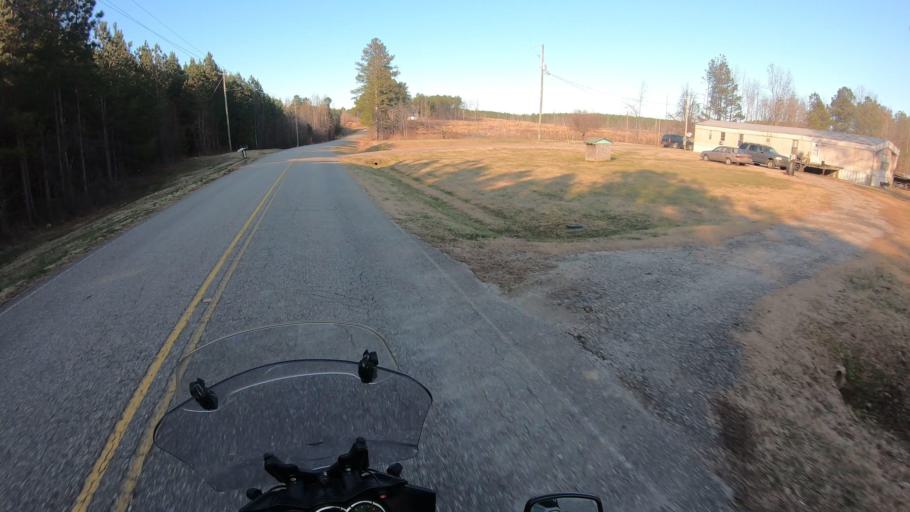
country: US
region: Alabama
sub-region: Cleburne County
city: Heflin
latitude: 33.7676
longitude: -85.4605
